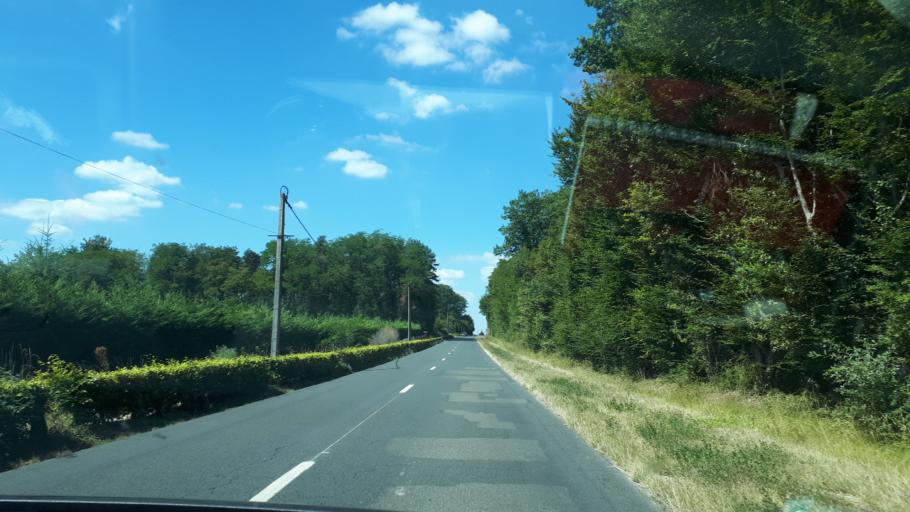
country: FR
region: Centre
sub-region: Departement du Loir-et-Cher
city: Mont-pres-Chambord
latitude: 47.5638
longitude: 1.4743
